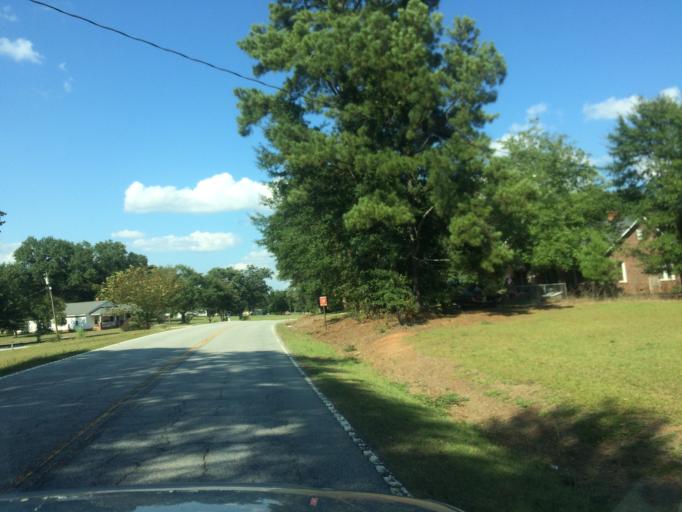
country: US
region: South Carolina
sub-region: Greenwood County
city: Ware Shoals
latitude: 34.4441
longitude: -82.2126
